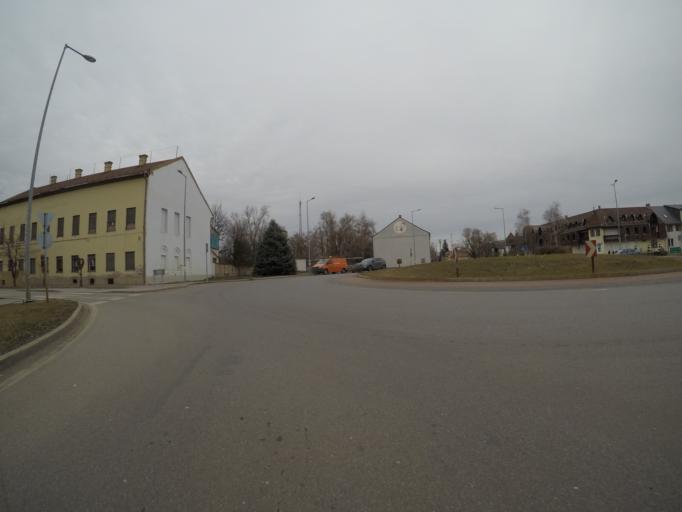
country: HU
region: Jasz-Nagykun-Szolnok
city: Jaszapati
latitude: 47.5136
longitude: 20.1401
